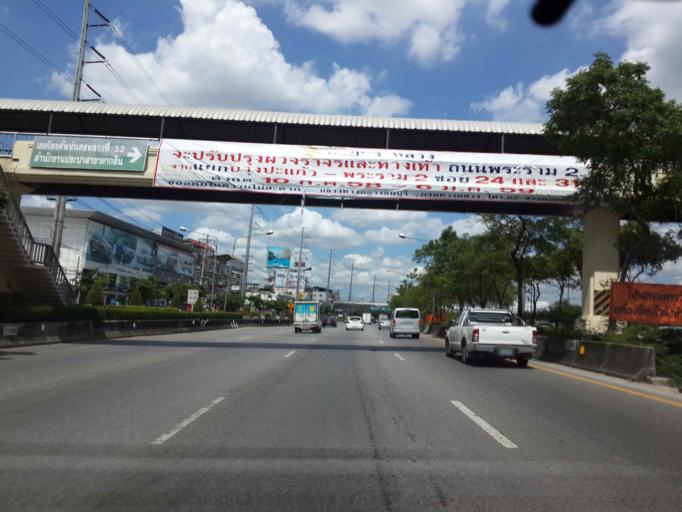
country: TH
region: Bangkok
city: Chom Thong
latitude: 13.6784
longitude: 100.4657
